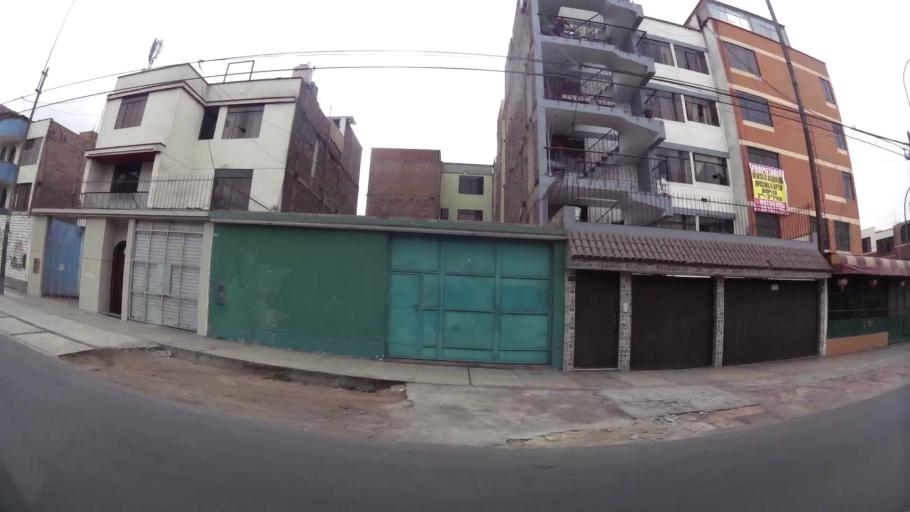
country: PE
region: Lima
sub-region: Lima
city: Surco
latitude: -12.1425
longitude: -76.9849
